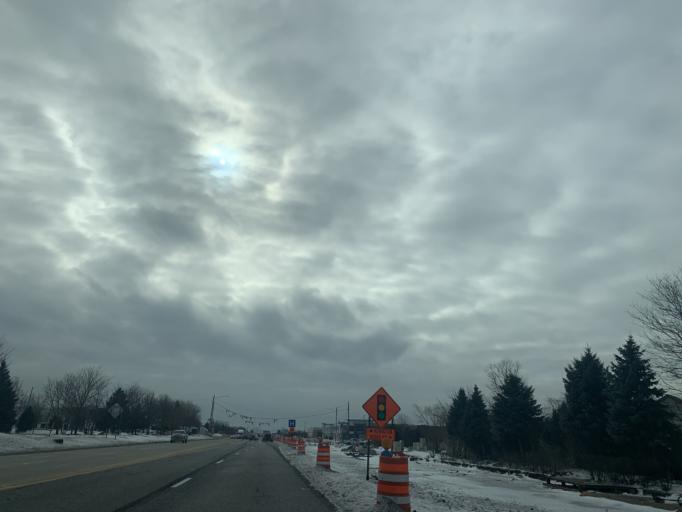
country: US
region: Illinois
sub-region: Will County
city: Romeoville
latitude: 41.6702
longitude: -88.1254
